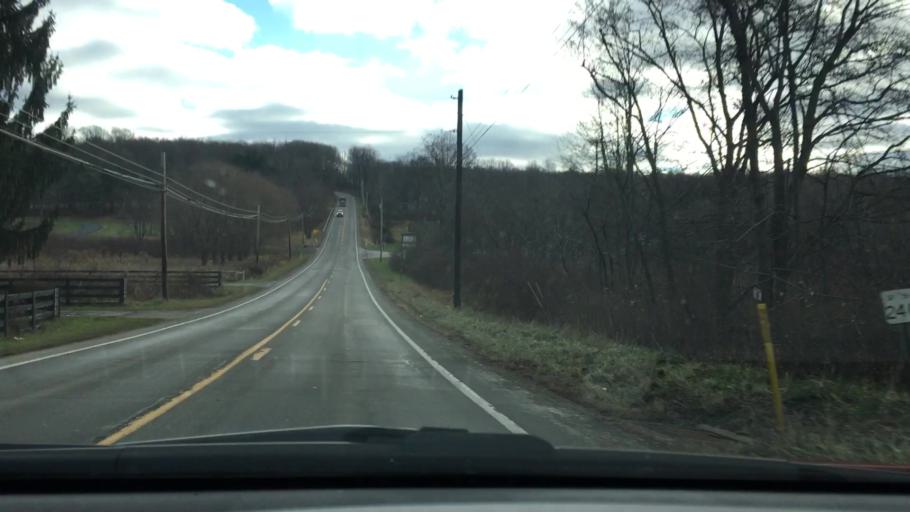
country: US
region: Pennsylvania
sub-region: Armstrong County
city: Orchard Hills
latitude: 40.6056
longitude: -79.4686
